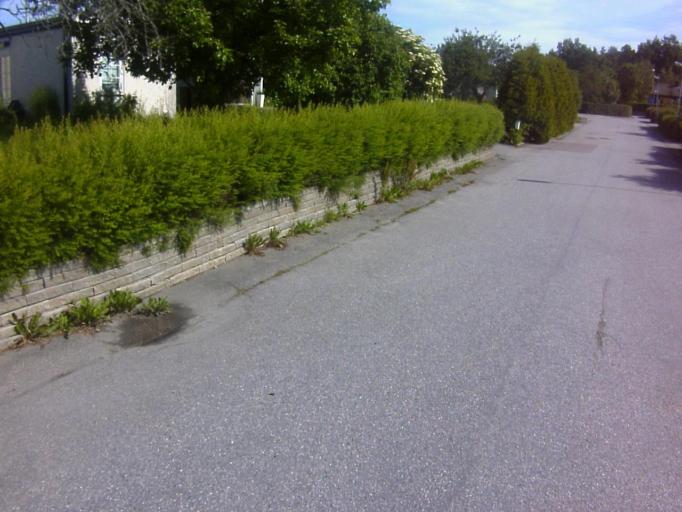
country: SE
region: Soedermanland
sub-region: Eskilstuna Kommun
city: Skogstorp
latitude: 59.3498
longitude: 16.4549
